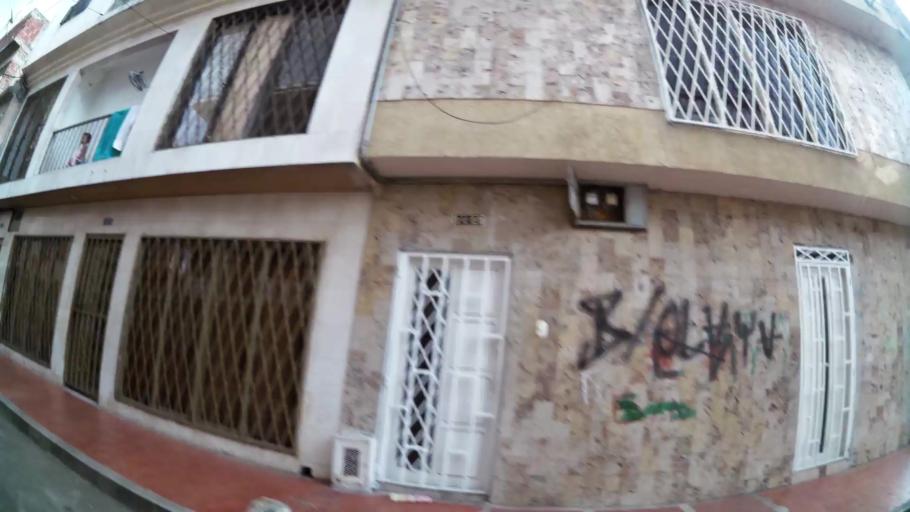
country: CO
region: Valle del Cauca
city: Cali
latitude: 3.4717
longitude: -76.5107
